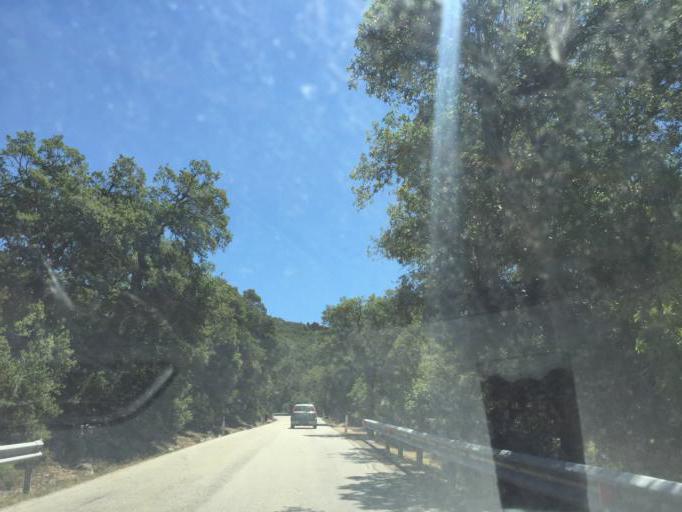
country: IT
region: Sardinia
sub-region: Provincia di Olbia-Tempio
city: Calangianus
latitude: 40.8999
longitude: 9.2223
